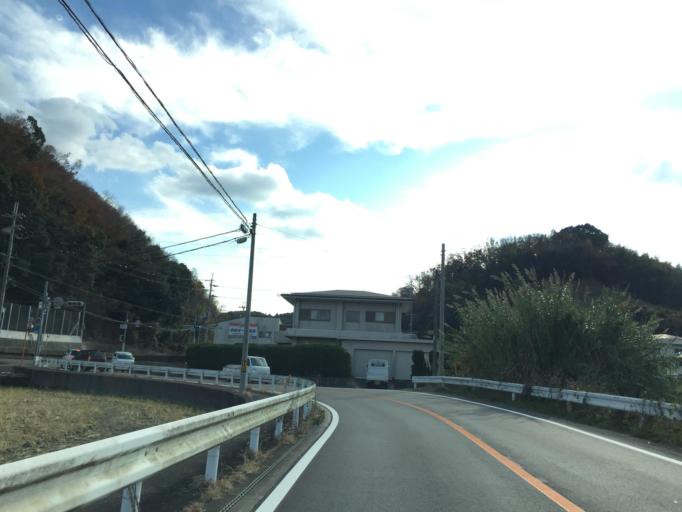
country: JP
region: Wakayama
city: Kainan
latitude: 34.1665
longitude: 135.2511
